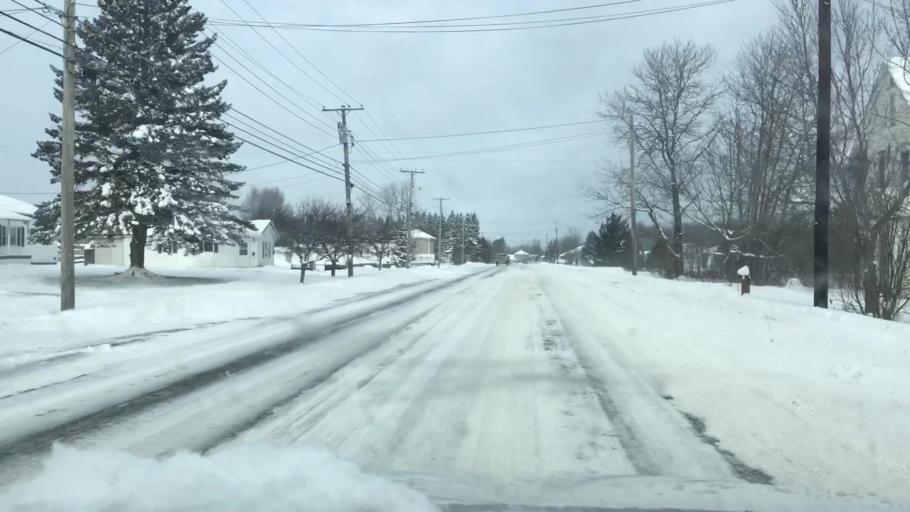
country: US
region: Maine
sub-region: Aroostook County
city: Van Buren
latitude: 47.1731
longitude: -67.9462
